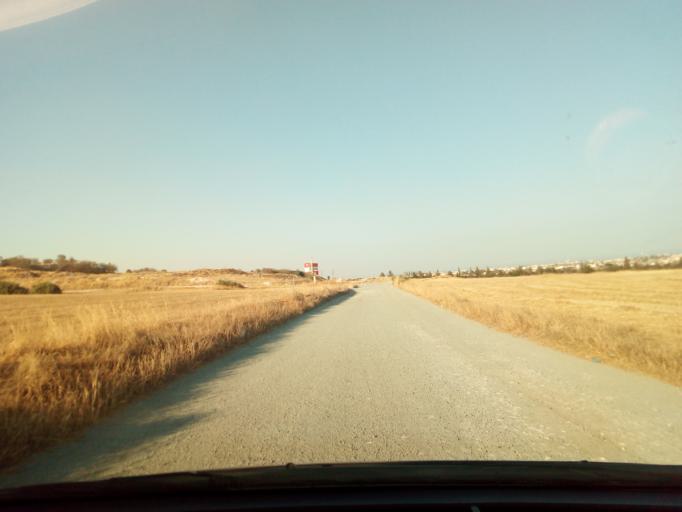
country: CY
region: Larnaka
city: Aradippou
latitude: 34.9252
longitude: 33.5636
